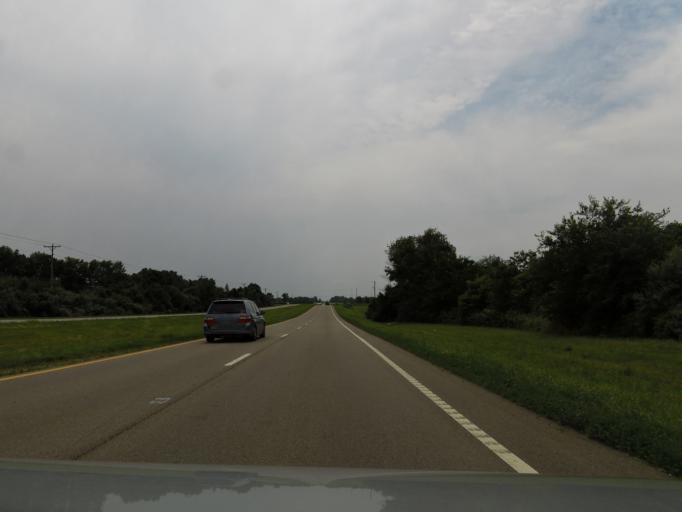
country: US
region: Ohio
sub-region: Greene County
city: Xenia
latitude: 39.6397
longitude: -83.9712
